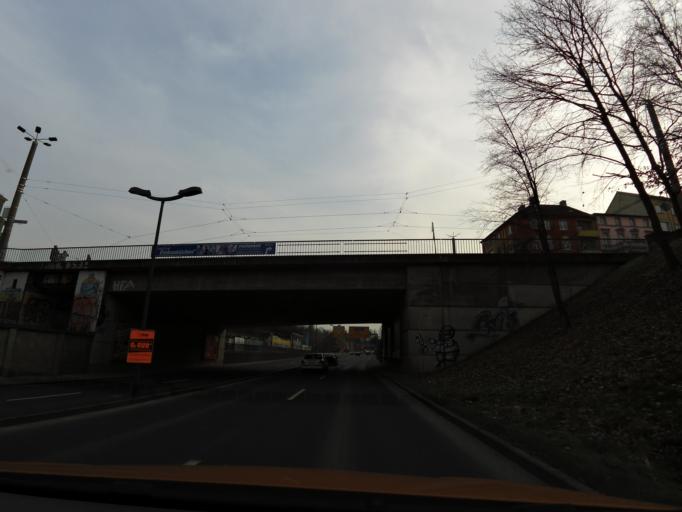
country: DE
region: Brandenburg
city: Frankfurt (Oder)
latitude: 52.3434
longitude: 14.5402
